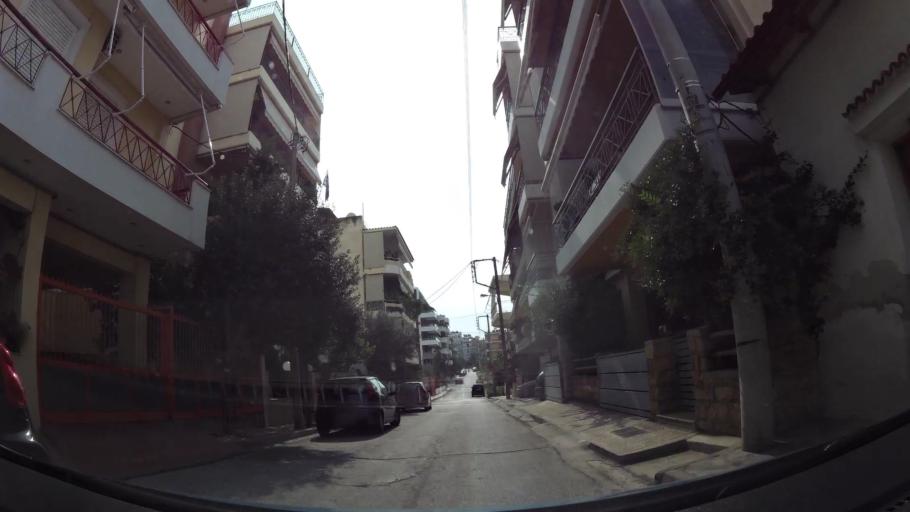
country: GR
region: Attica
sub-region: Nomarchia Athinas
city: Agios Dimitrios
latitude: 37.9269
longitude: 23.7278
